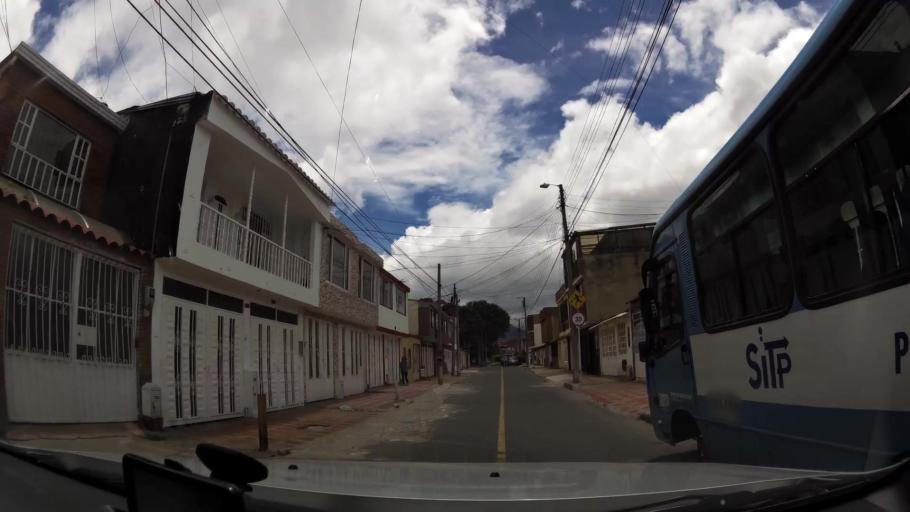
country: CO
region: Bogota D.C.
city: Bogota
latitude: 4.6095
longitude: -74.1198
